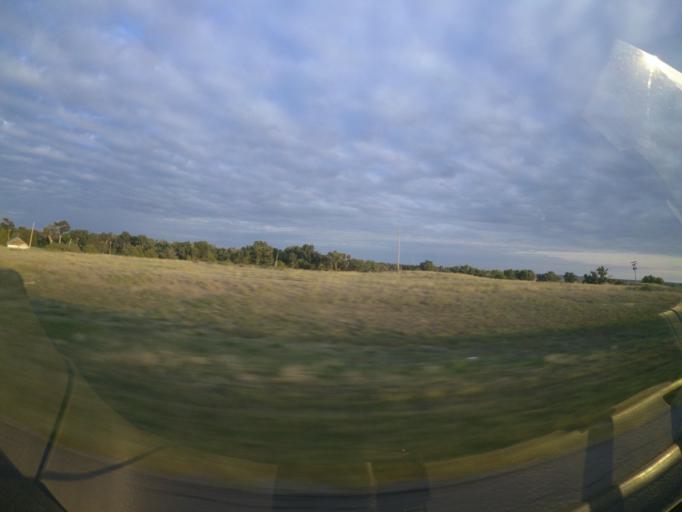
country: US
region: Kansas
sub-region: Cheyenne County
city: Saint Francis
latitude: 39.7662
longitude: -101.8422
